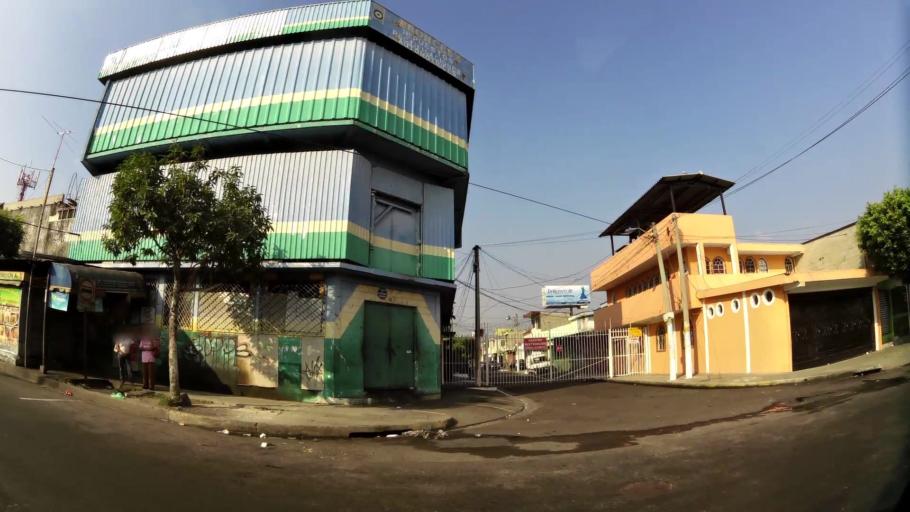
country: SV
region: San Salvador
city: San Salvador
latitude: 13.6840
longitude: -89.2192
